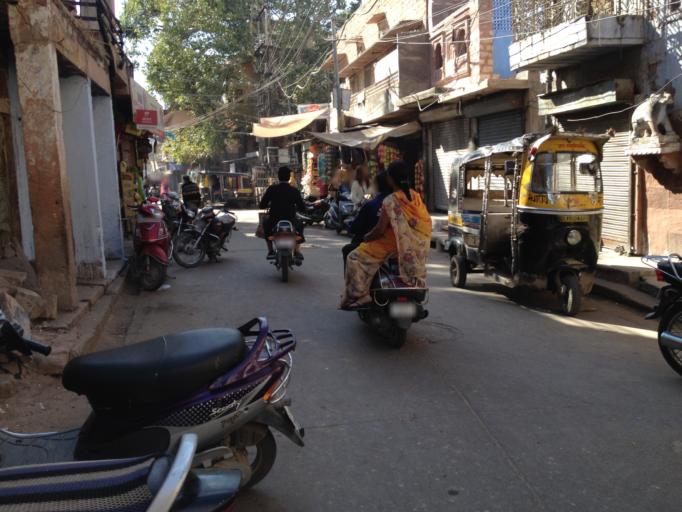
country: IN
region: Rajasthan
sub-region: Jodhpur
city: Jodhpur
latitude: 26.2959
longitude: 73.0143
